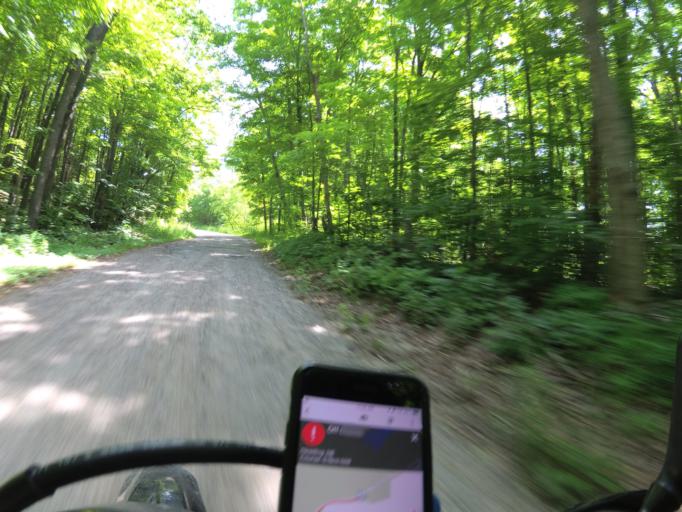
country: CA
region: Ontario
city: Skatepark
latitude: 44.7356
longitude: -76.8432
